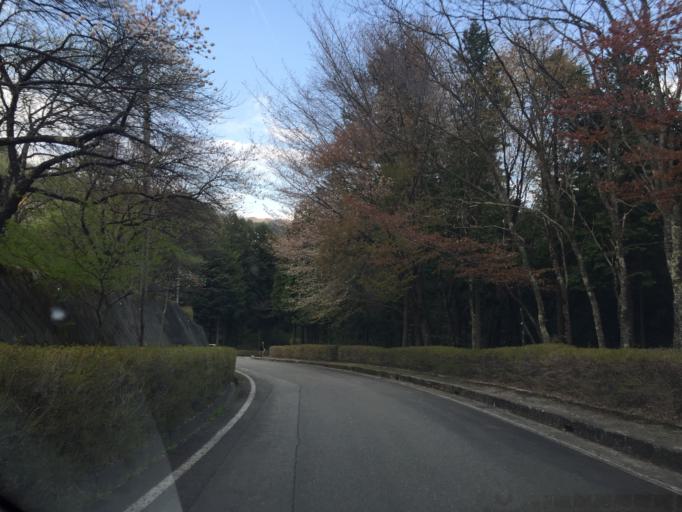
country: JP
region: Nagano
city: Iida
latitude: 35.5120
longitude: 137.6649
